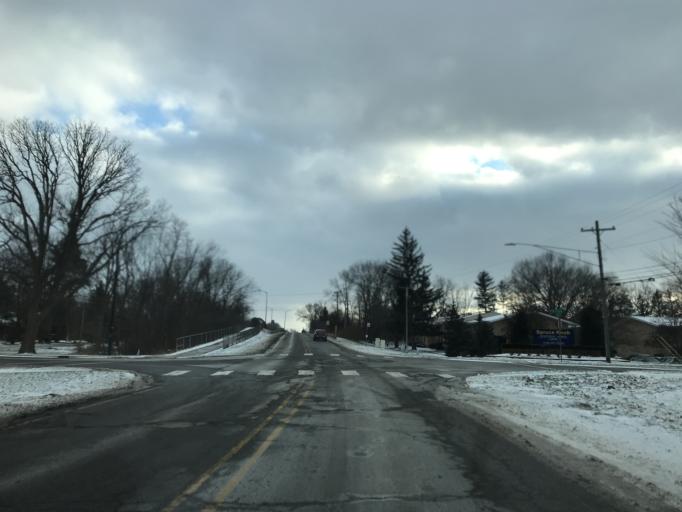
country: US
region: Michigan
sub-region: Washtenaw County
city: Ann Arbor
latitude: 42.2393
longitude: -83.7201
